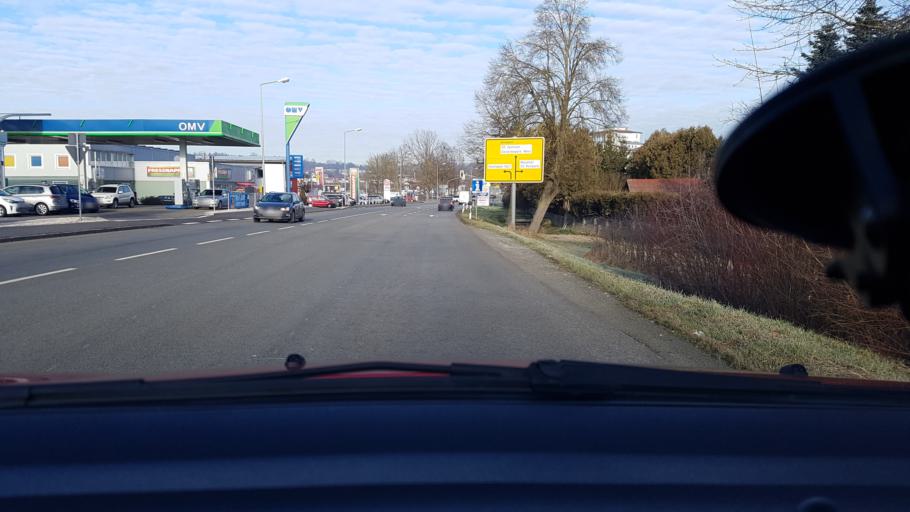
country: DE
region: Bavaria
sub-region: Lower Bavaria
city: Pfarrkirchen
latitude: 48.4211
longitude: 12.9429
